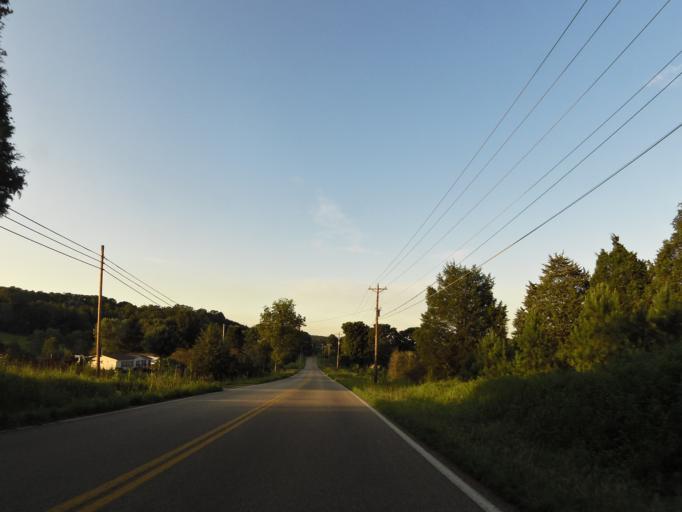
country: US
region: Tennessee
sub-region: Roane County
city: Midtown
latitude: 35.7930
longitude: -84.5716
